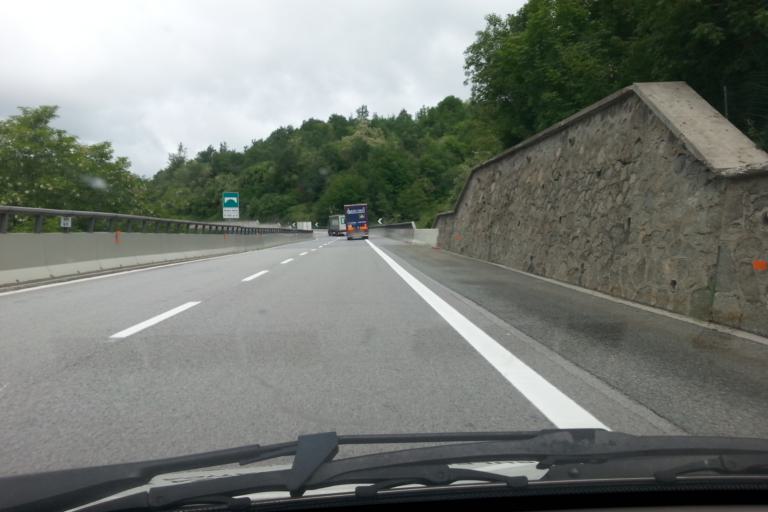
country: IT
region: Liguria
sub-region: Provincia di Savona
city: Valzemola
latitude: 44.3596
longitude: 8.1638
